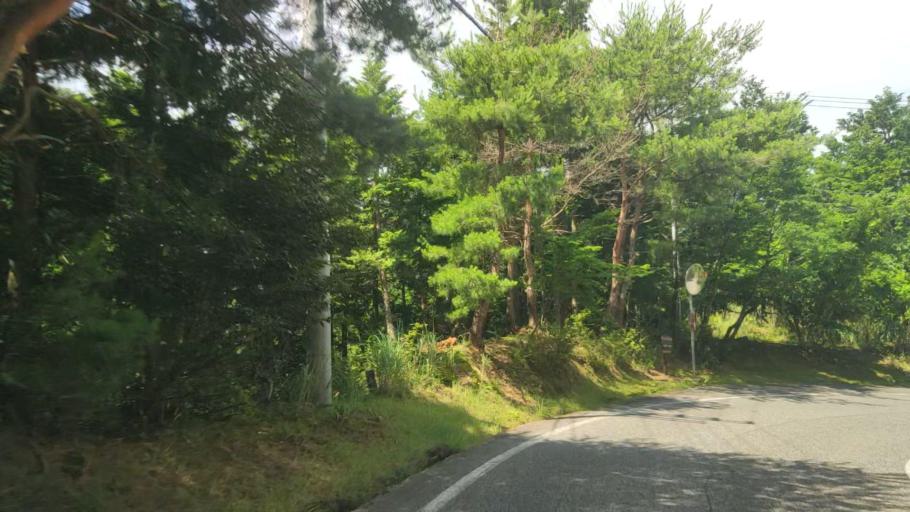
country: JP
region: Hyogo
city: Toyooka
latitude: 35.6383
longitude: 134.7710
